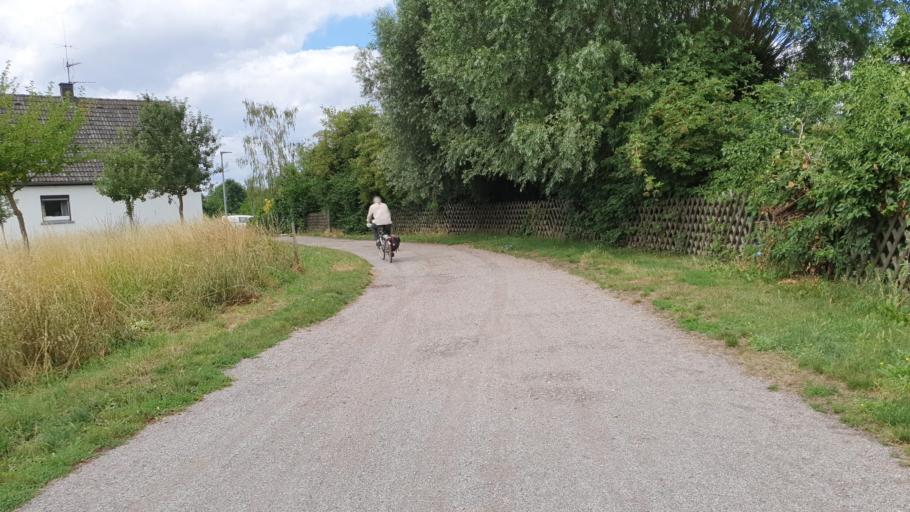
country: DE
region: Rheinland-Pfalz
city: Speyer
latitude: 49.3293
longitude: 8.4410
